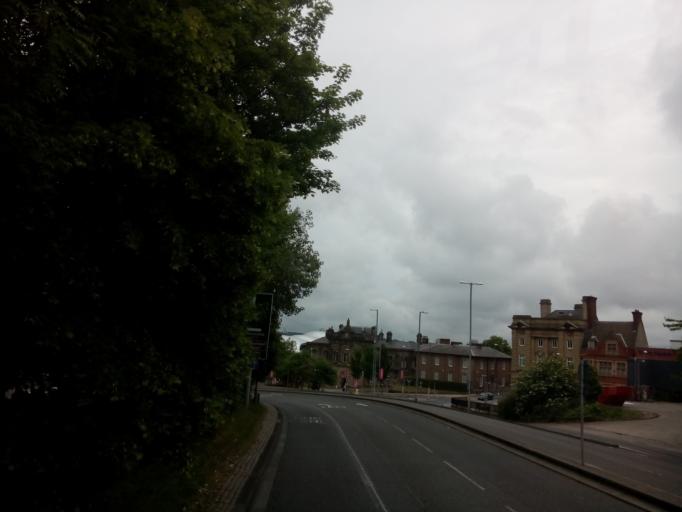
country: GB
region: England
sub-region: Gateshead
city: Gateshead
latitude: 54.9629
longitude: -1.6052
